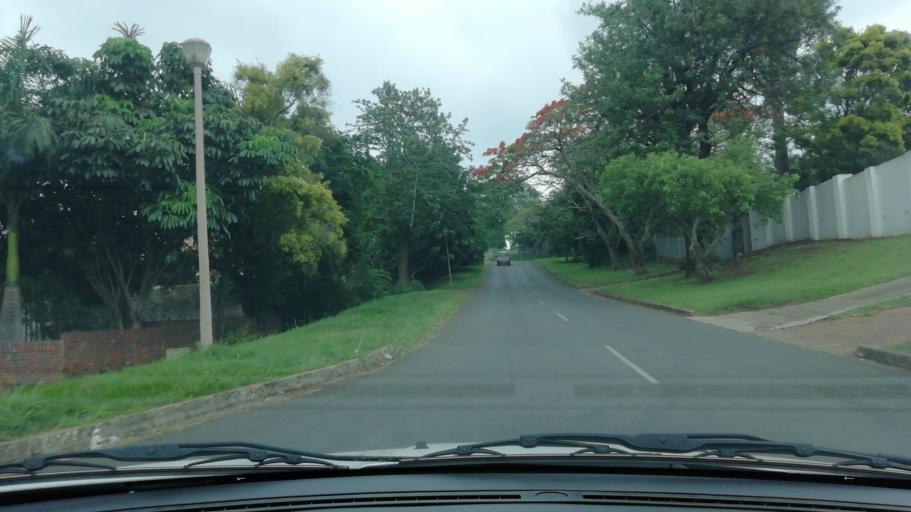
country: ZA
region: KwaZulu-Natal
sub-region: uThungulu District Municipality
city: Empangeni
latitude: -28.7571
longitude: 31.8850
